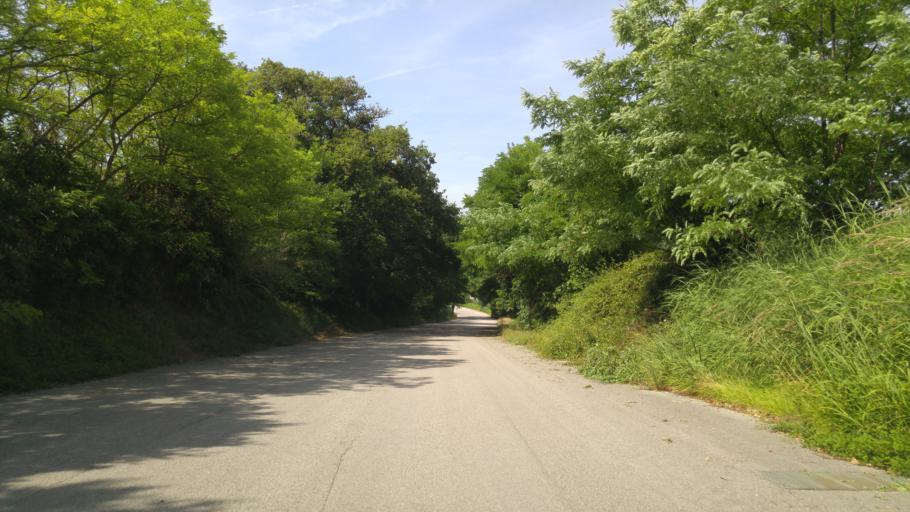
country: IT
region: The Marches
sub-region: Provincia di Pesaro e Urbino
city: Fenile
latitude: 43.8453
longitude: 12.9770
